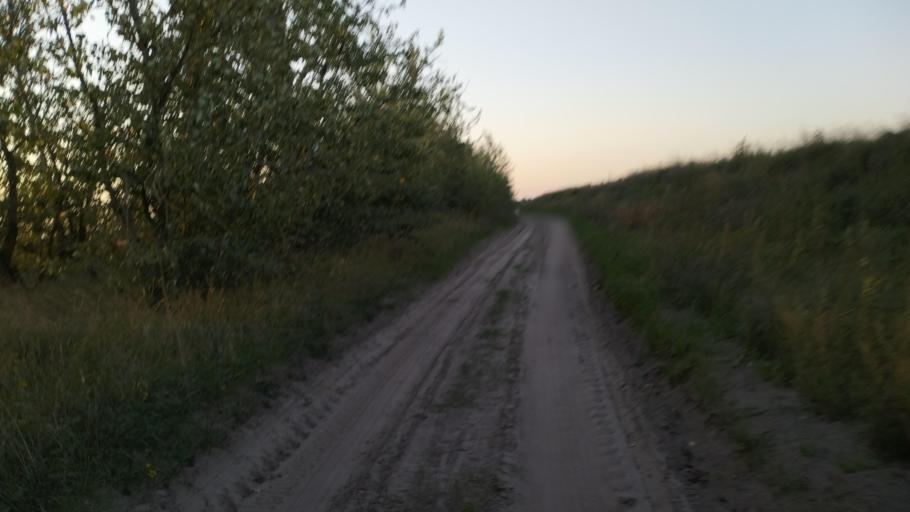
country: BY
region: Brest
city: Davyd-Haradok
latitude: 52.0312
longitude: 27.1938
